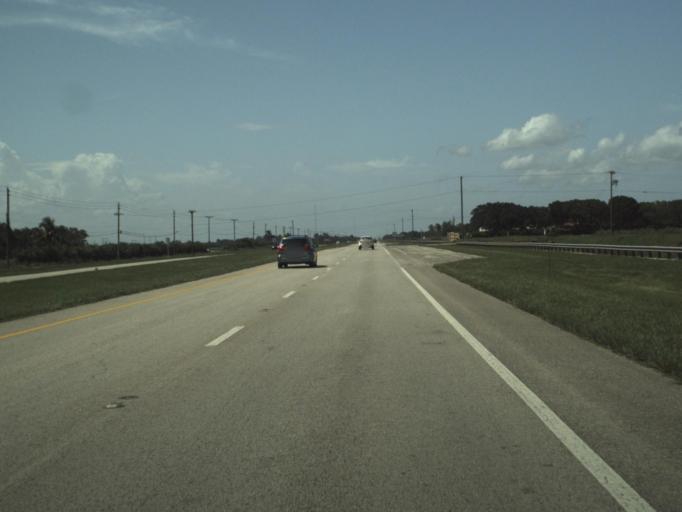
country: US
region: Florida
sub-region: Palm Beach County
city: Villages of Oriole
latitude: 26.4997
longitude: -80.2050
